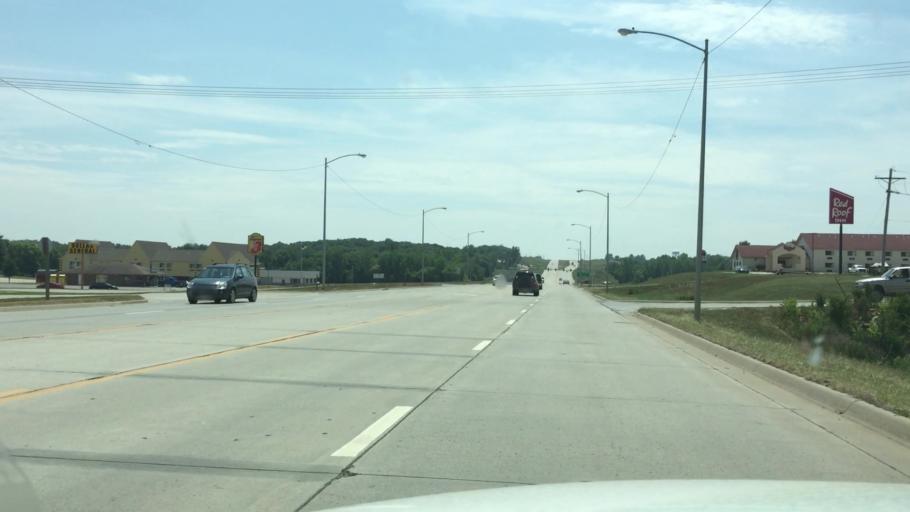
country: US
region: Kansas
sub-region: Jackson County
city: Holton
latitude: 39.4597
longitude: -95.7480
